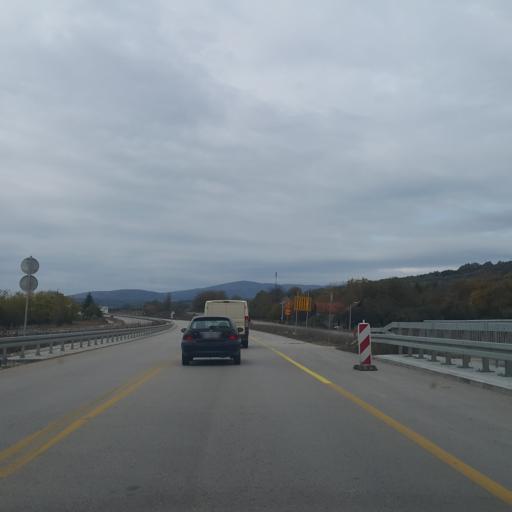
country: RS
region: Central Serbia
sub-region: Pirotski Okrug
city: Pirot
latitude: 43.2203
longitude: 22.4957
